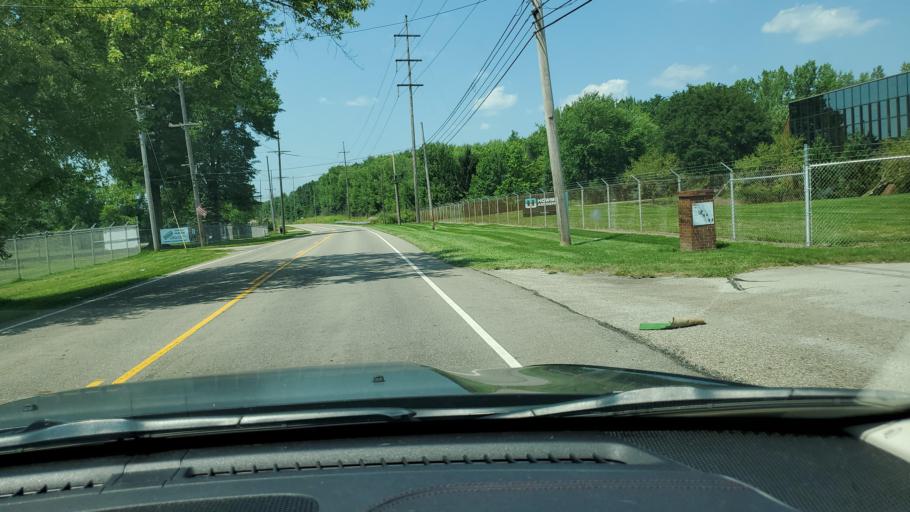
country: US
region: Ohio
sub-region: Trumbull County
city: Bolindale
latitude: 41.1904
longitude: -80.7855
